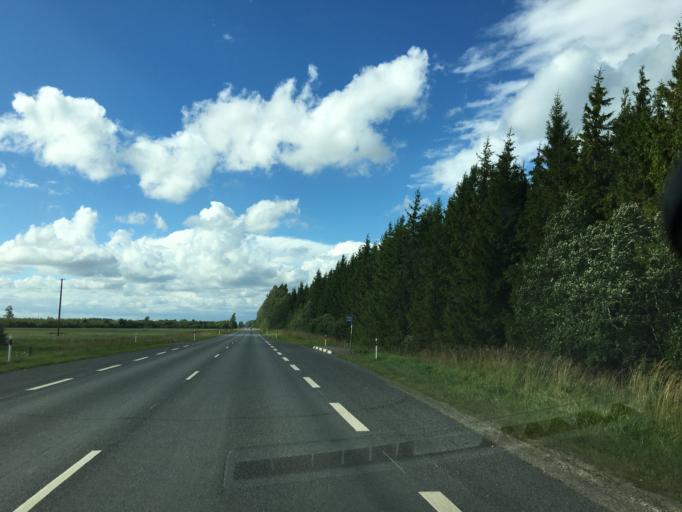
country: EE
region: Paernumaa
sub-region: Vaendra vald (alev)
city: Vandra
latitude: 58.5951
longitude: 25.1509
